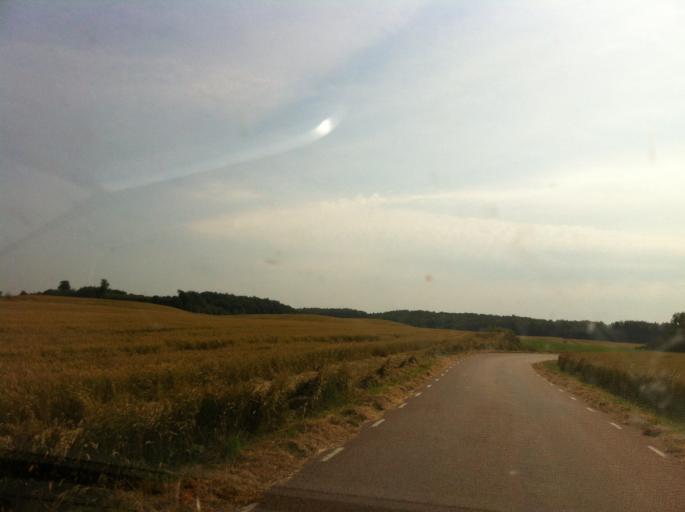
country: SE
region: Skane
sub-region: Eslovs Kommun
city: Stehag
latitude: 55.9609
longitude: 13.3176
